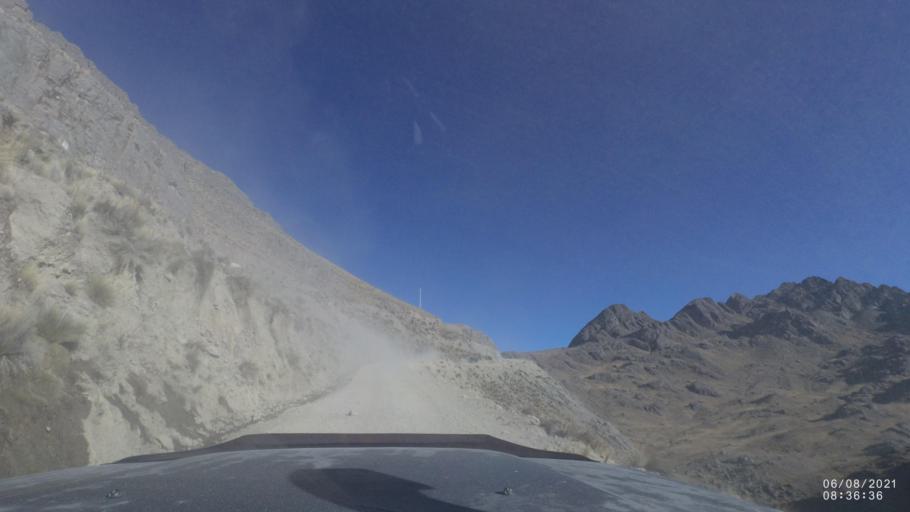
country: BO
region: Cochabamba
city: Sipe Sipe
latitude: -17.1771
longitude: -66.3854
